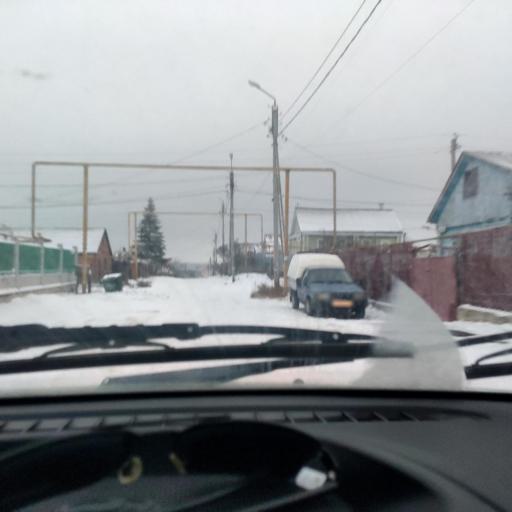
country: RU
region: Samara
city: Zhigulevsk
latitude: 53.4873
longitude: 49.5306
